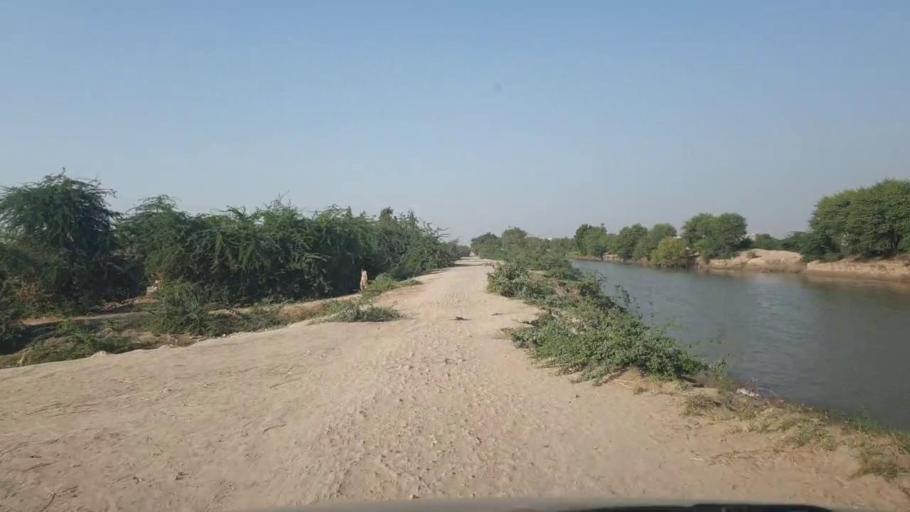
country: PK
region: Sindh
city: Badin
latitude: 24.6494
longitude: 68.8152
